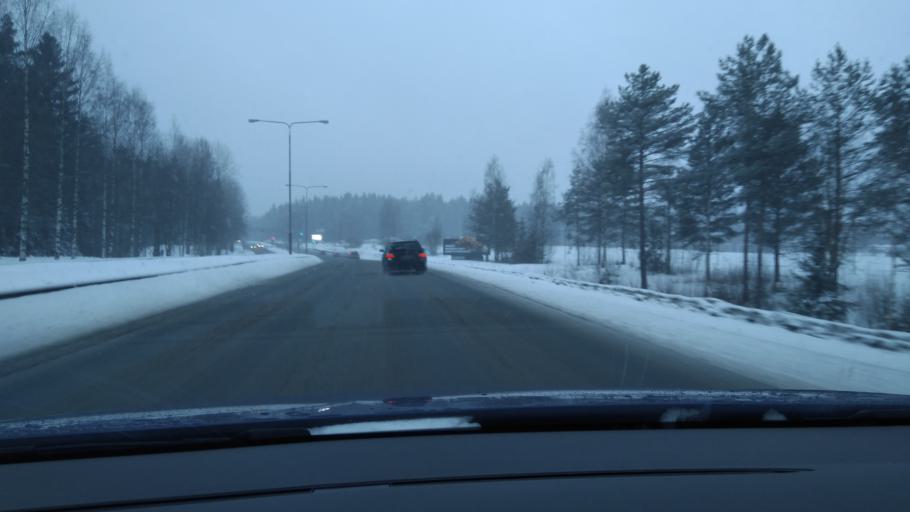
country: FI
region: Pirkanmaa
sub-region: Tampere
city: Tampere
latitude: 61.5047
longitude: 23.8509
